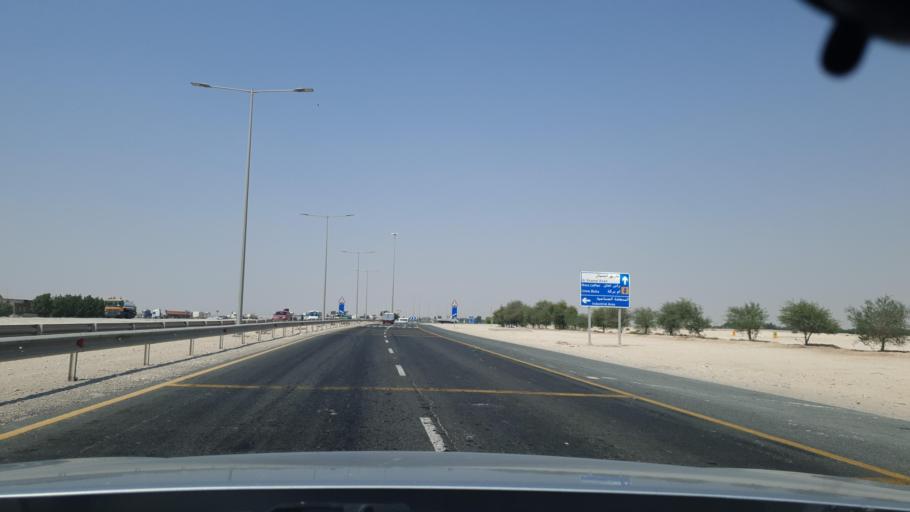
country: QA
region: Al Khawr
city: Al Khawr
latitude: 25.7197
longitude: 51.5014
